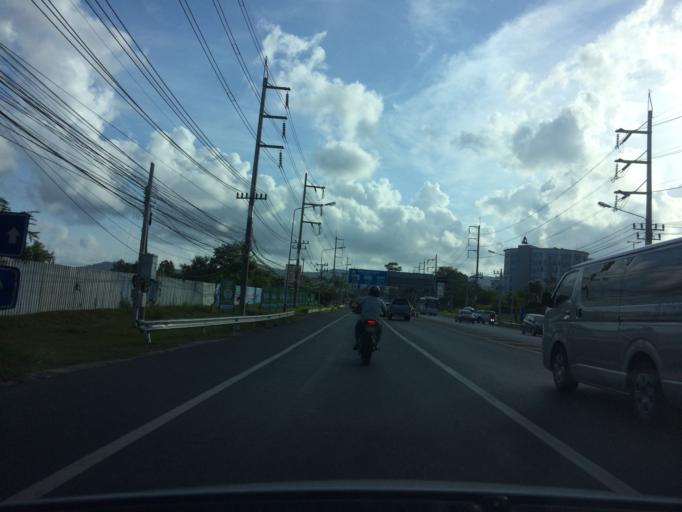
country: TH
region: Phuket
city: Mueang Phuket
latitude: 7.8726
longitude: 98.3629
